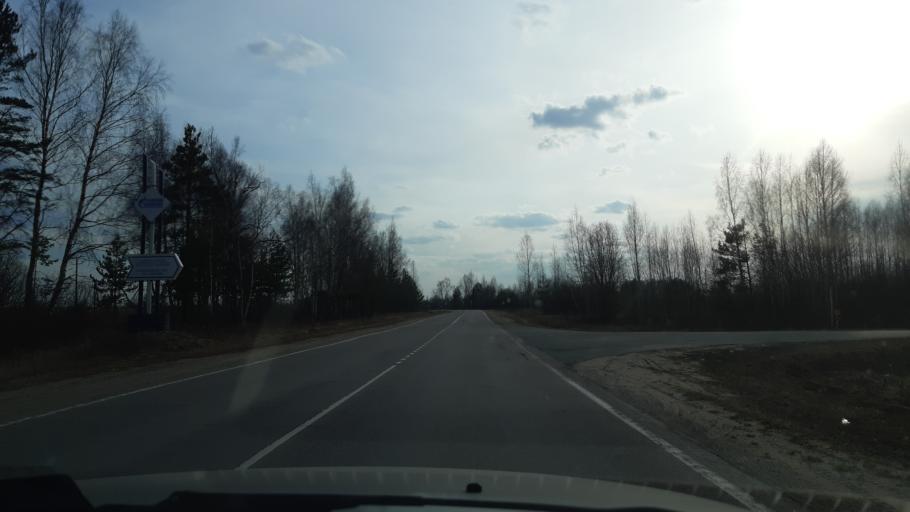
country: RU
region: Vladimir
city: Luknovo
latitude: 56.1765
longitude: 42.0061
